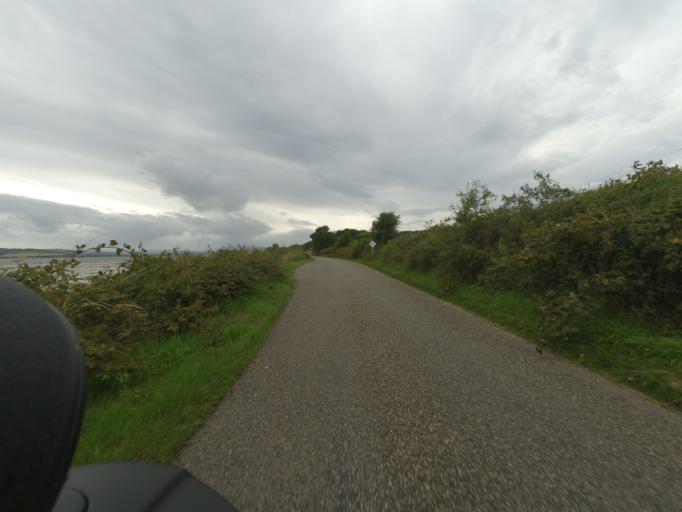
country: GB
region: Scotland
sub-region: Highland
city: Inverness
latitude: 57.5045
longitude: -4.2777
